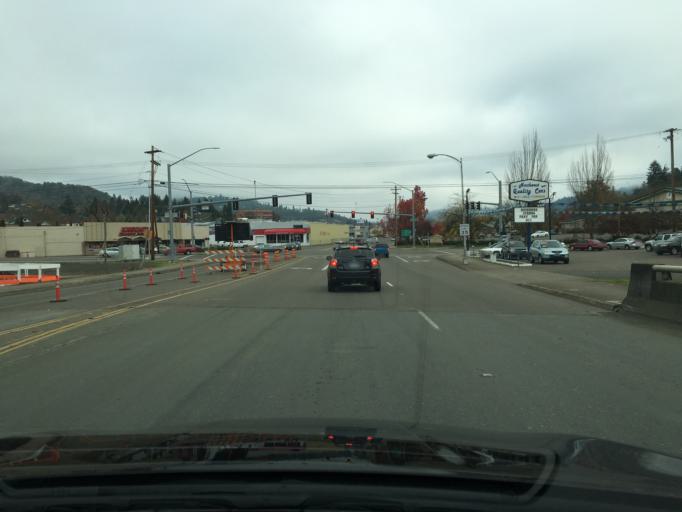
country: US
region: Oregon
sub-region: Douglas County
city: Roseburg
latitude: 43.2134
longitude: -123.3423
